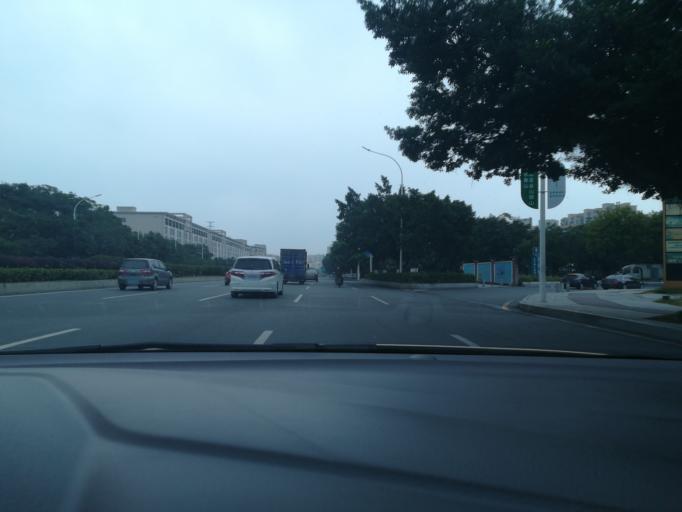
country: CN
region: Guangdong
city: Nansha
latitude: 22.8031
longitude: 113.5357
